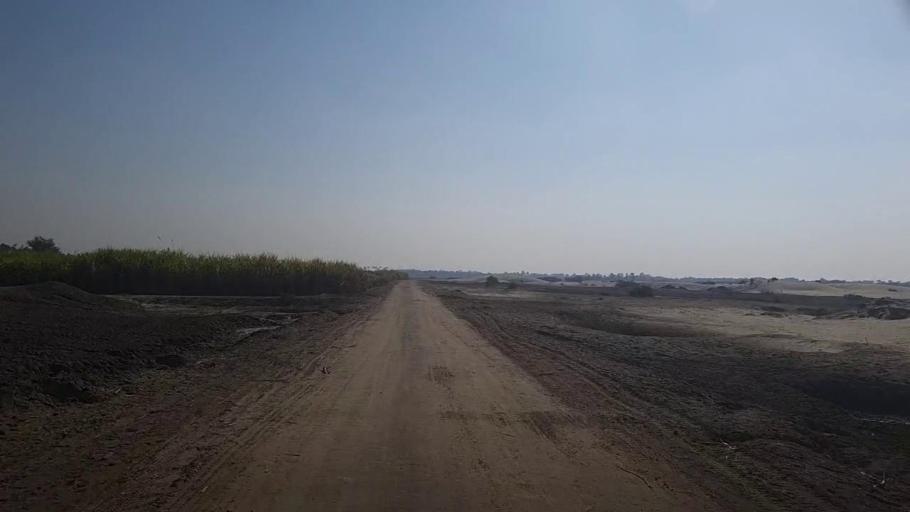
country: PK
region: Sindh
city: Kot Diji
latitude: 27.4365
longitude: 68.7278
